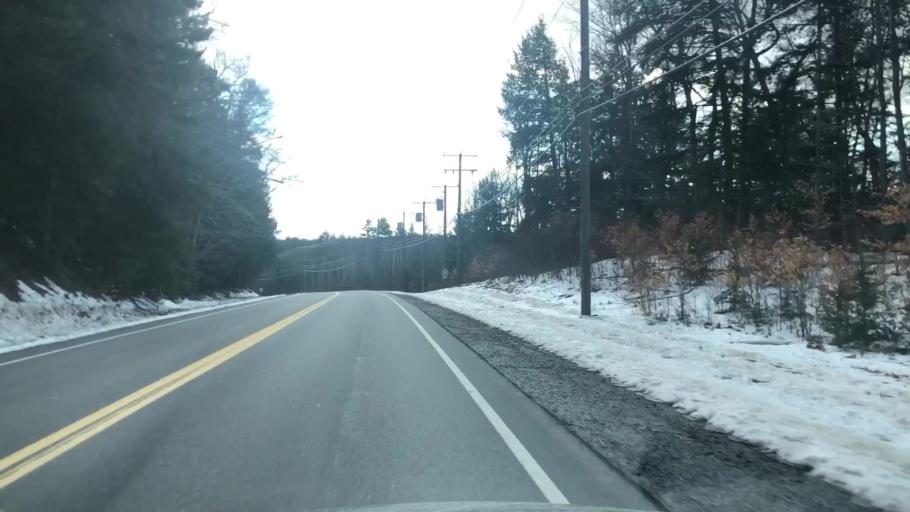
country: US
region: New Hampshire
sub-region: Hillsborough County
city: Mont Vernon
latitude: 42.8706
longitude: -71.6691
